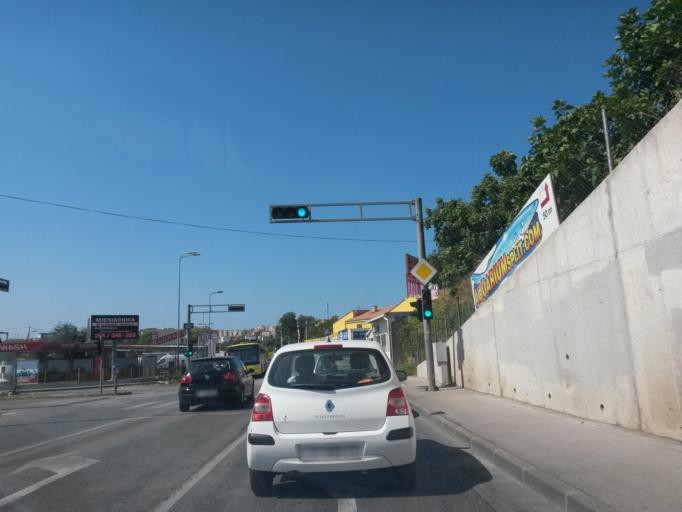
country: HR
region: Splitsko-Dalmatinska
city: Solin
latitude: 43.5310
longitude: 16.4851
